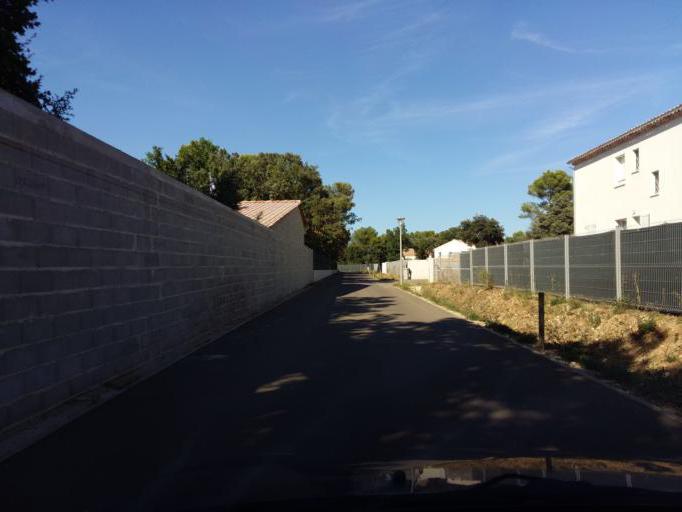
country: FR
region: Provence-Alpes-Cote d'Azur
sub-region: Departement du Vaucluse
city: Saint-Didier
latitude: 44.0202
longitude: 5.0976
